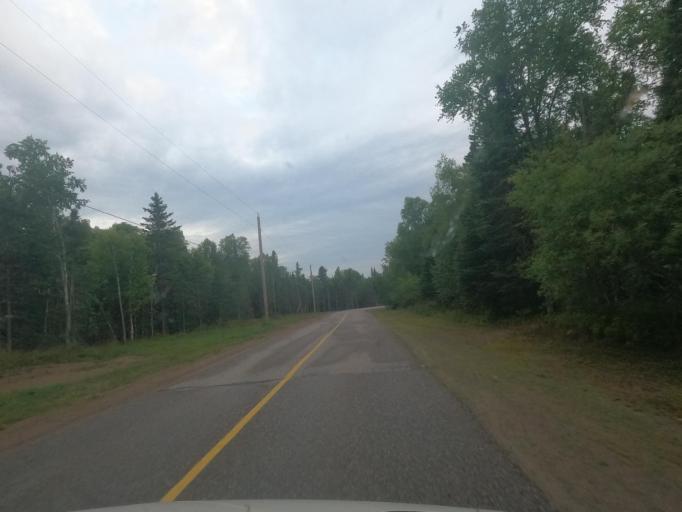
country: CA
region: Ontario
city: Marathon
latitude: 48.7736
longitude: -87.1110
